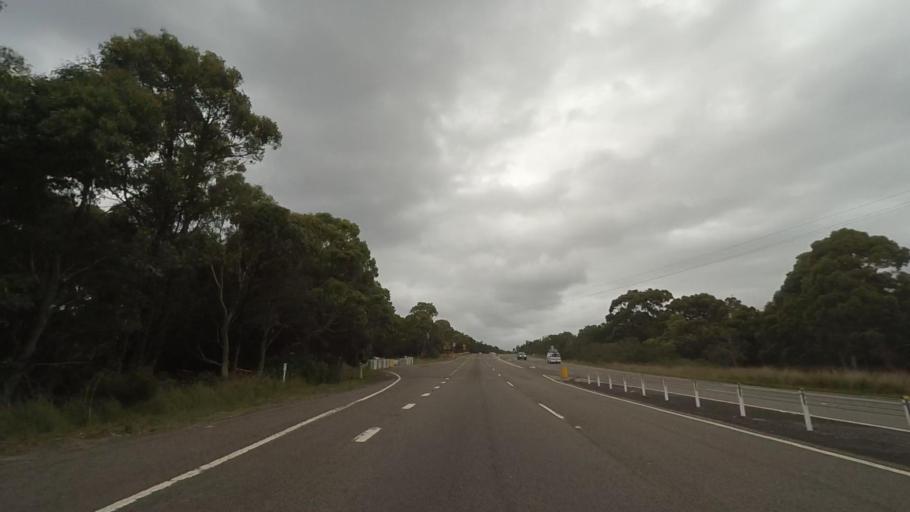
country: AU
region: New South Wales
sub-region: Lake Macquarie Shire
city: Belmont South
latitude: -33.1240
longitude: 151.6313
